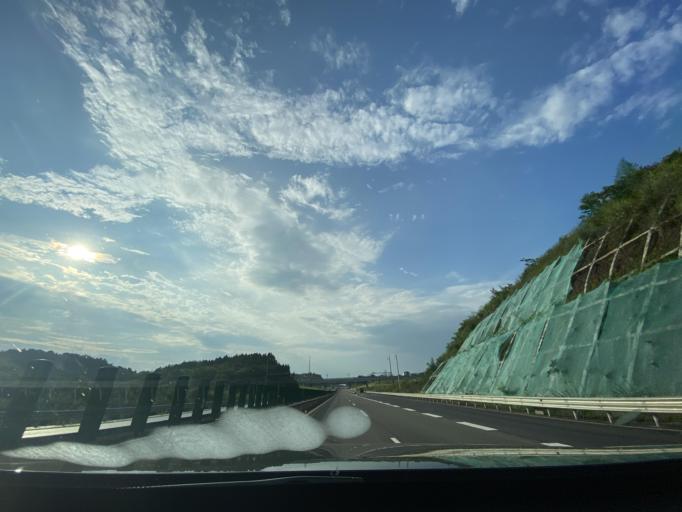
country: CN
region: Sichuan
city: Jiancheng
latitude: 30.3592
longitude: 104.5278
